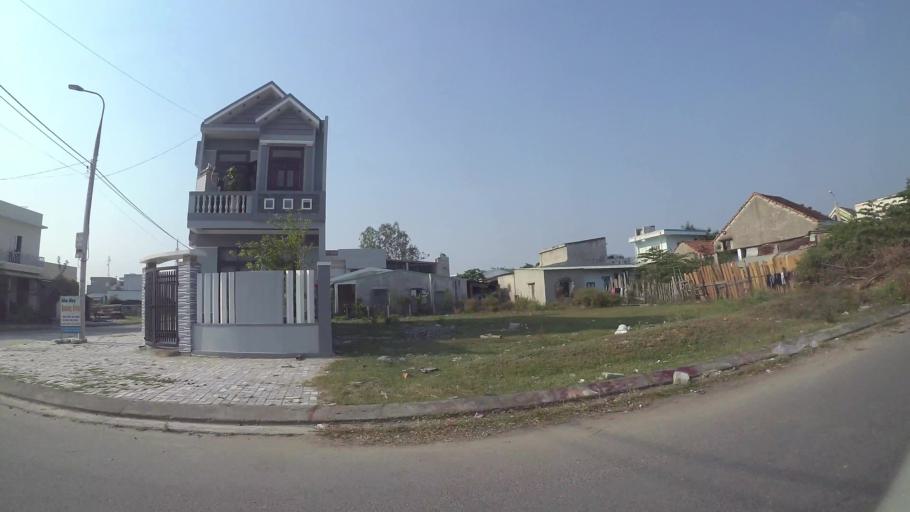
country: VN
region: Da Nang
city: Ngu Hanh Son
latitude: 15.9532
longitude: 108.2573
